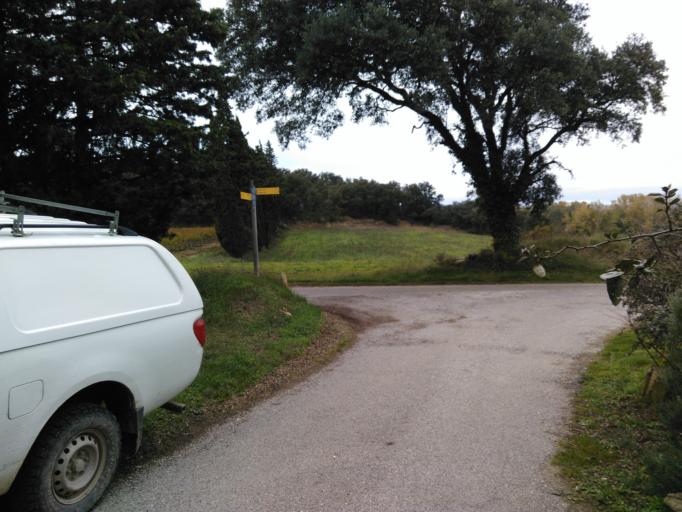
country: FR
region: Rhone-Alpes
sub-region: Departement de la Drome
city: Montsegur-sur-Lauzon
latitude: 44.3484
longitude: 4.8746
